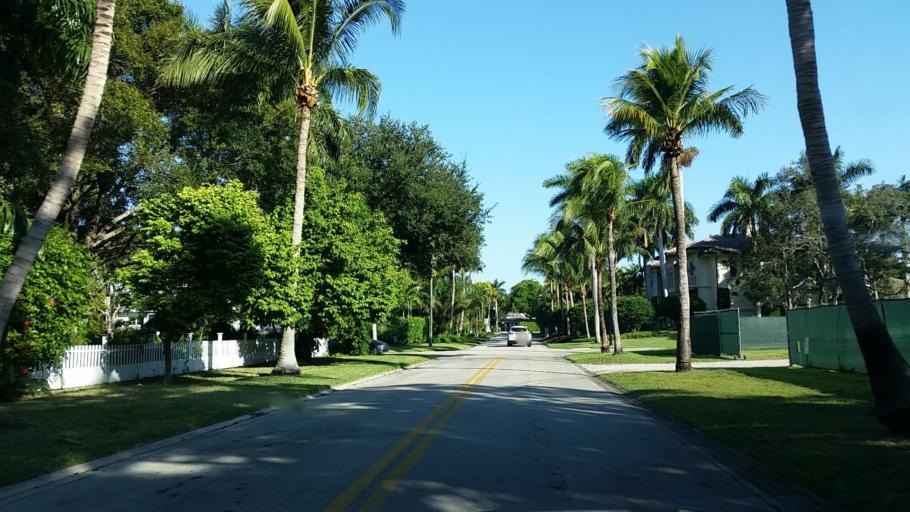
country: US
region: Florida
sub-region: Collier County
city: Naples
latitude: 26.1445
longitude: -81.8050
